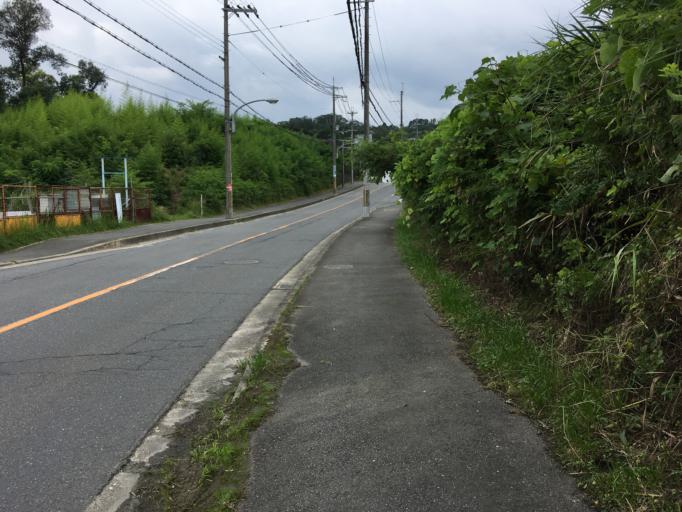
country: JP
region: Nara
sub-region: Ikoma-shi
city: Ikoma
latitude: 34.6645
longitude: 135.7176
